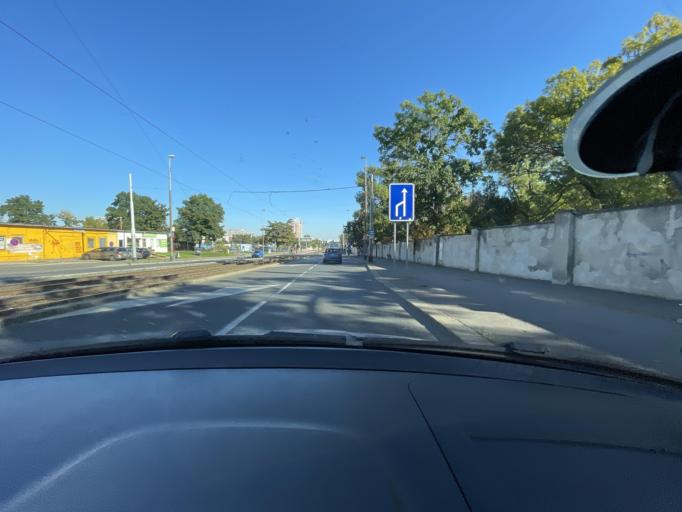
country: CZ
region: Praha
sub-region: Praha 8
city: Liben
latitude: 50.0778
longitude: 14.4789
